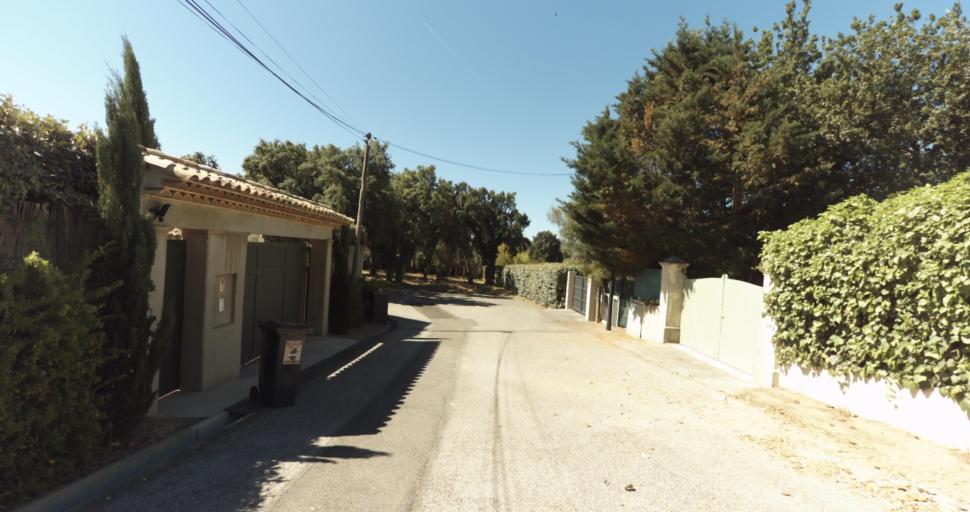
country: FR
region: Provence-Alpes-Cote d'Azur
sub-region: Departement du Var
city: Gassin
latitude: 43.2569
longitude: 6.6035
